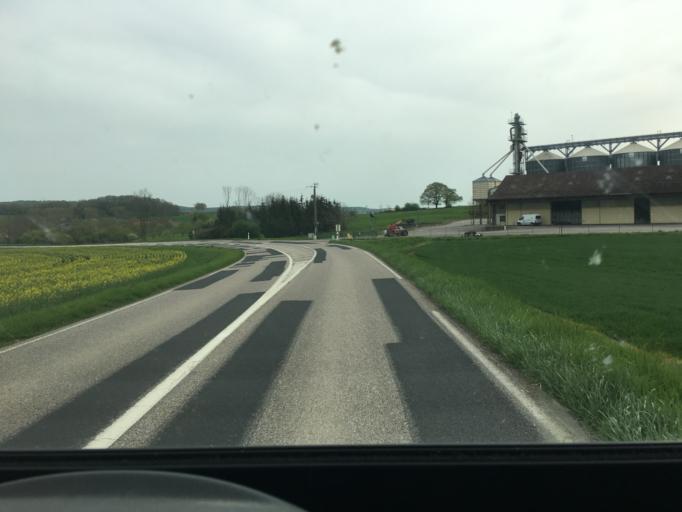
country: FR
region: Lorraine
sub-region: Departement de Meurthe-et-Moselle
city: Einville-au-Jard
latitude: 48.6742
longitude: 6.4894
